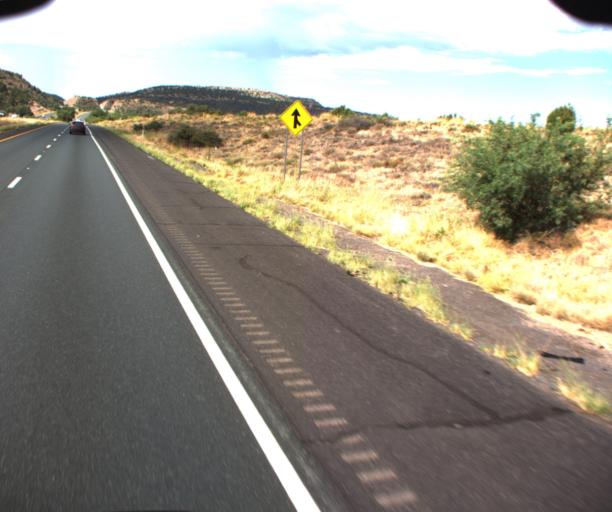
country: US
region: Arizona
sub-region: Yavapai County
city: Camp Verde
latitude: 34.5142
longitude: -111.9926
